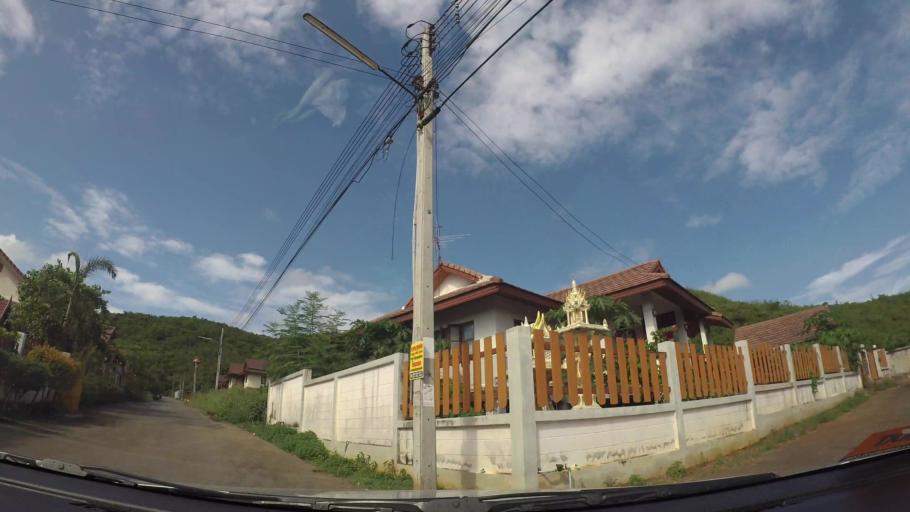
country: TH
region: Chon Buri
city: Sattahip
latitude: 12.6888
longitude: 100.9137
